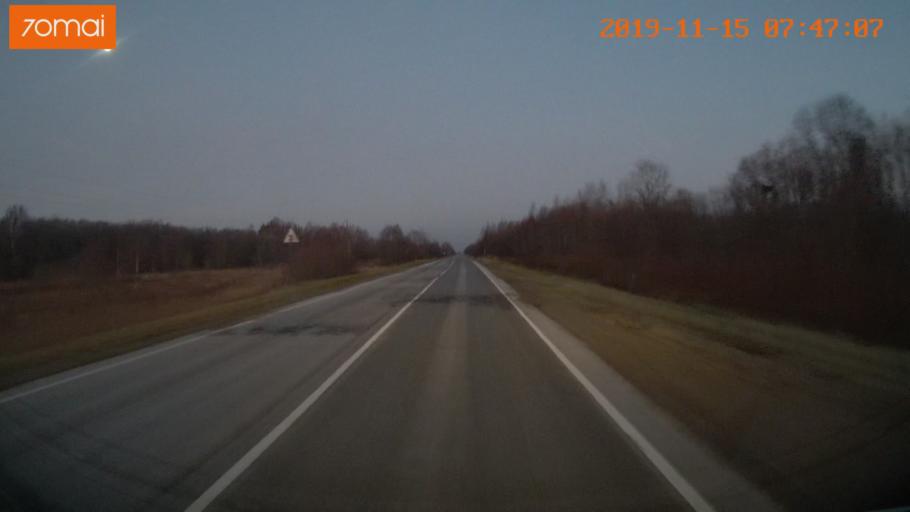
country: RU
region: Vologda
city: Sheksna
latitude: 58.8387
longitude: 38.2664
